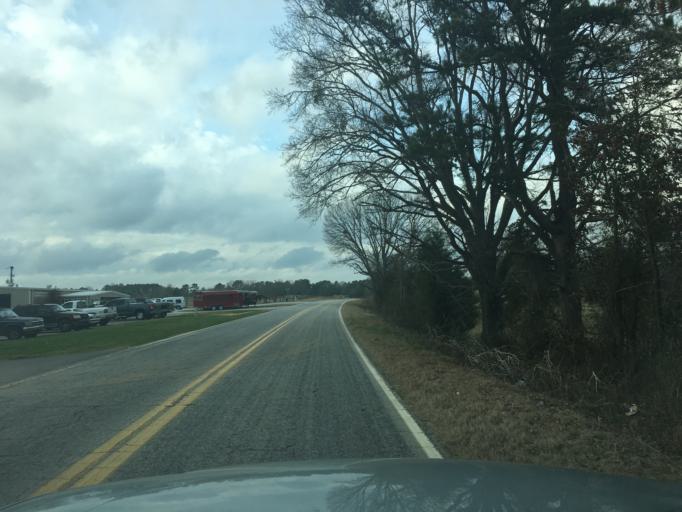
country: US
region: South Carolina
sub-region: Abbeville County
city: Abbeville
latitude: 34.2300
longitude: -82.3917
